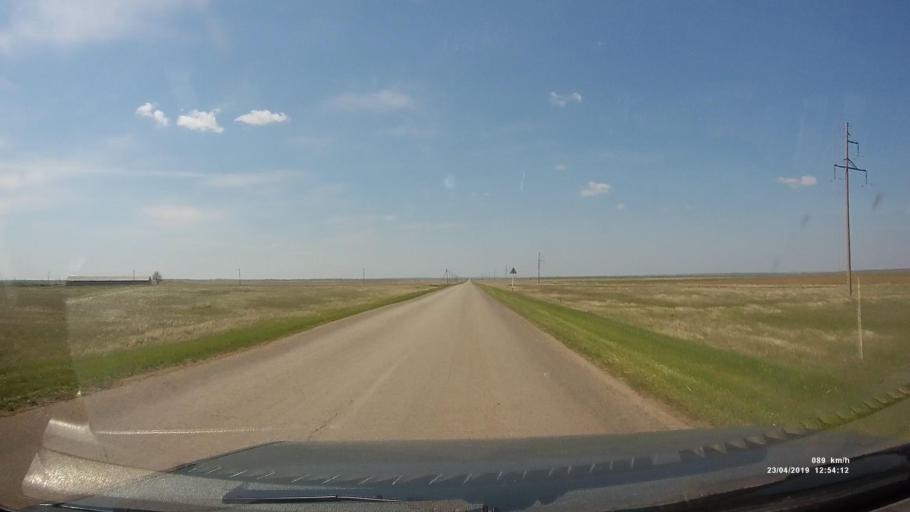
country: RU
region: Kalmykiya
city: Yashalta
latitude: 46.5786
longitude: 42.5826
